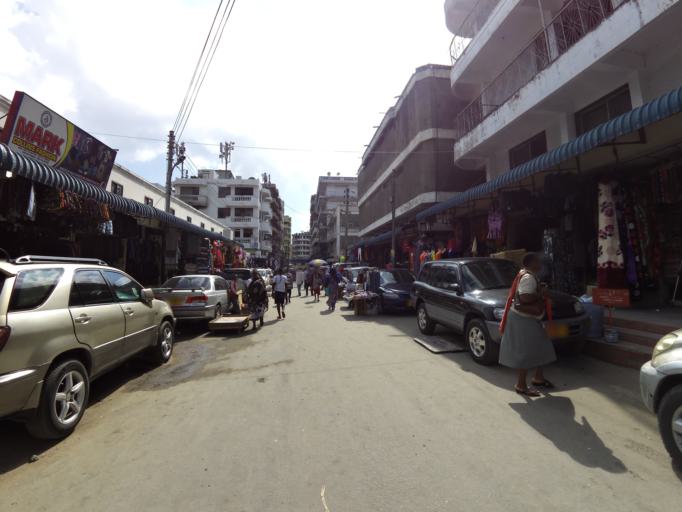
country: TZ
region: Dar es Salaam
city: Dar es Salaam
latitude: -6.8216
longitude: 39.2736
